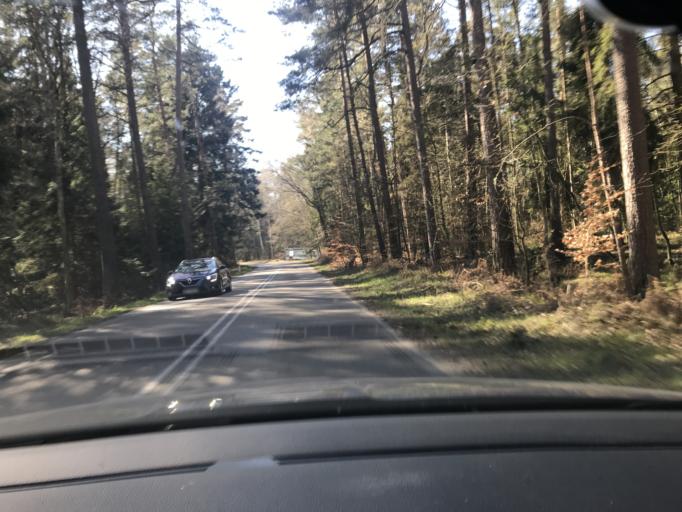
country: PL
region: Pomeranian Voivodeship
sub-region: Powiat nowodworski
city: Krynica Morska
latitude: 54.3678
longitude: 19.3870
